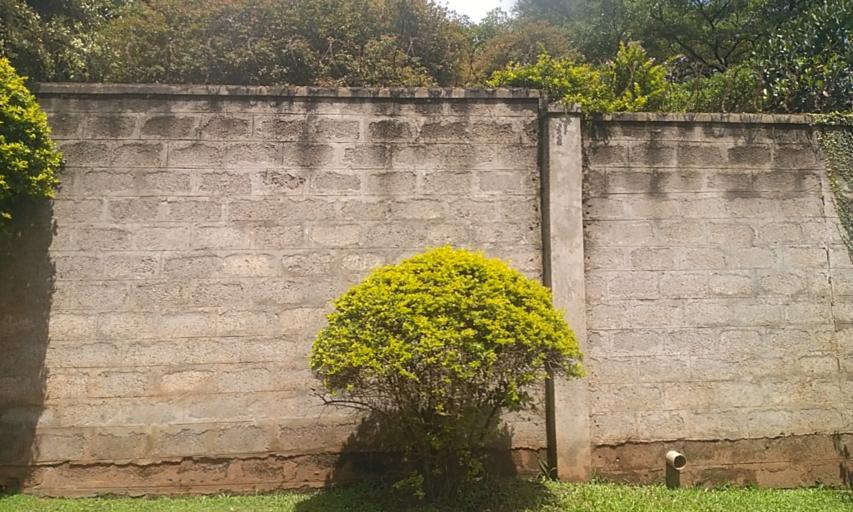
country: UG
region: Central Region
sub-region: Kampala District
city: Kampala
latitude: 0.3310
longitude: 32.5990
